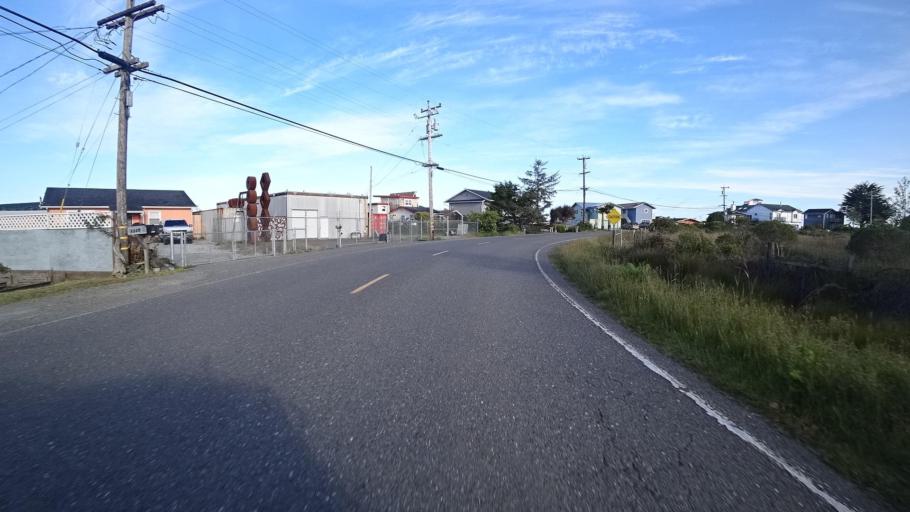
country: US
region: California
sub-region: Humboldt County
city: Humboldt Hill
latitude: 40.7403
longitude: -124.2149
